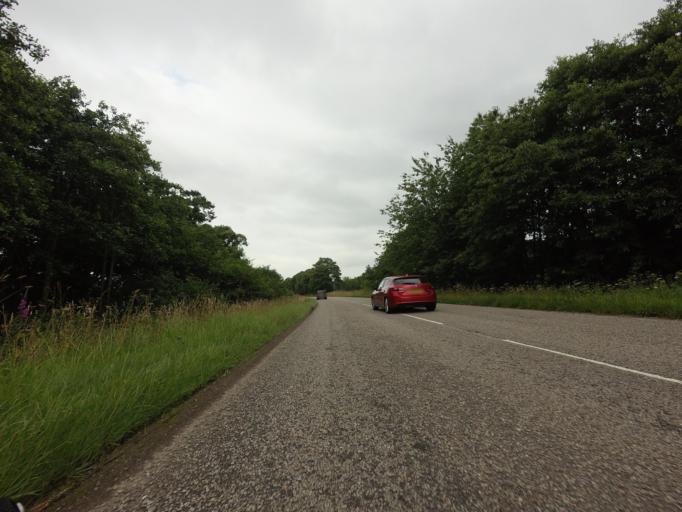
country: GB
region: Scotland
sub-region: Highland
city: Alness
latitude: 57.9109
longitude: -4.3733
